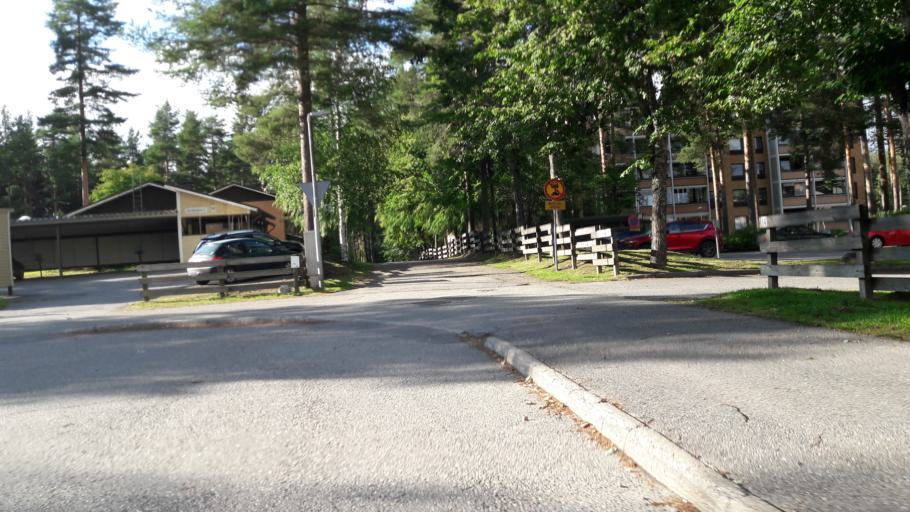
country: FI
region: North Karelia
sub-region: Joensuu
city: Joensuu
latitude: 62.6056
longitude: 29.7983
